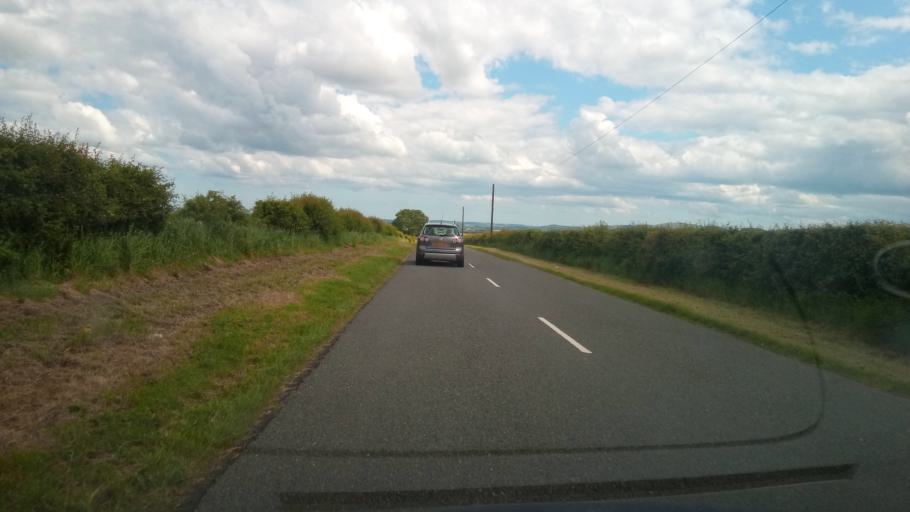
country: GB
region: Scotland
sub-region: The Scottish Borders
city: Coldstream
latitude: 55.6038
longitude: -2.3279
